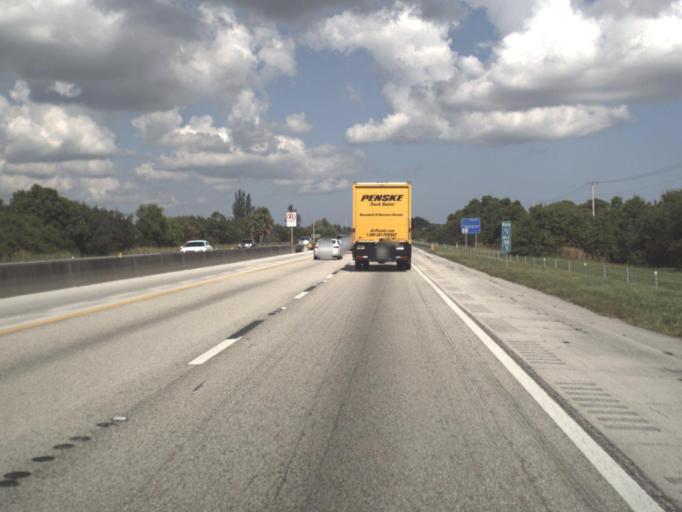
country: US
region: Florida
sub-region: Palm Beach County
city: Palm Beach Gardens
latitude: 26.8291
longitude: -80.1303
